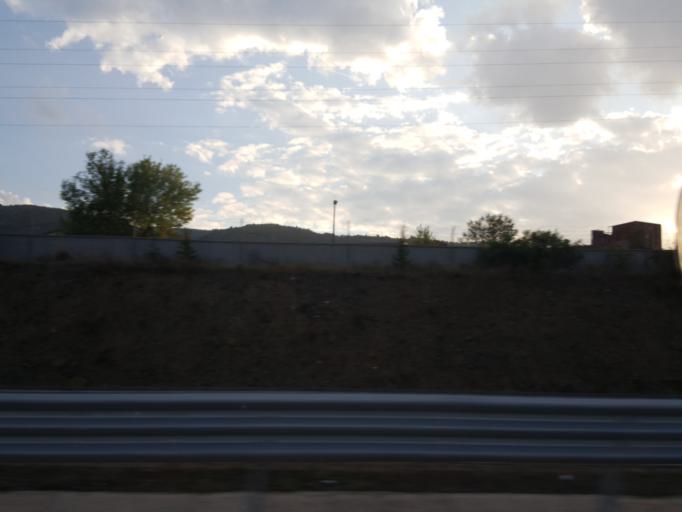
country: TR
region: Tokat
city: Niksar
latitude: 40.4980
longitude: 36.9249
